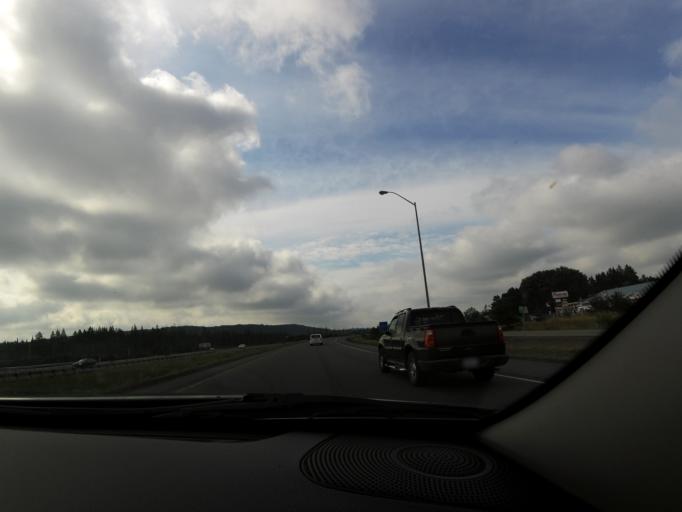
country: CA
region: Ontario
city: Huntsville
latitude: 45.4520
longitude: -79.2471
